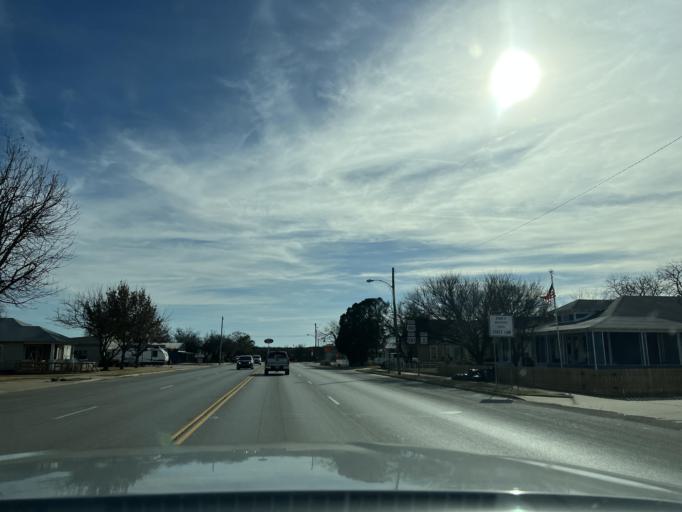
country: US
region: Texas
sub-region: Shackelford County
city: Albany
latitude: 32.7220
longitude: -99.2973
